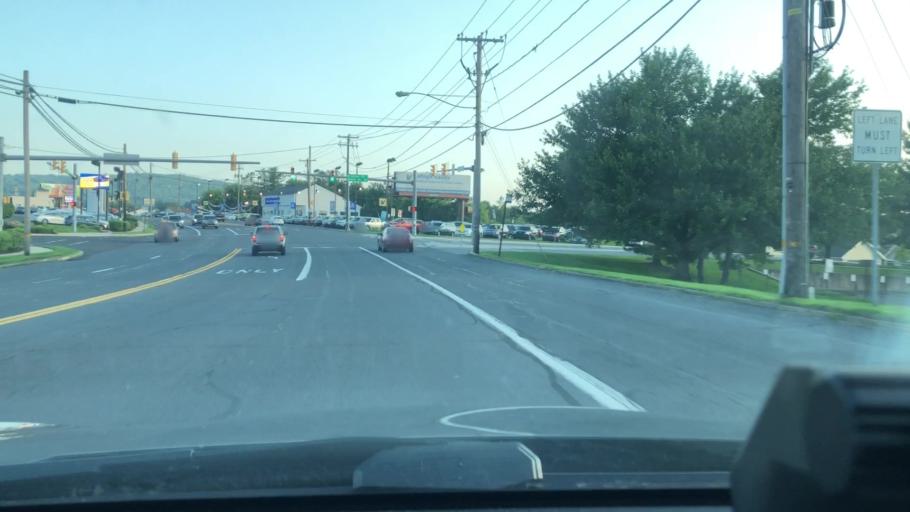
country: US
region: Pennsylvania
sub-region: Lehigh County
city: Emmaus
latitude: 40.5521
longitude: -75.4914
